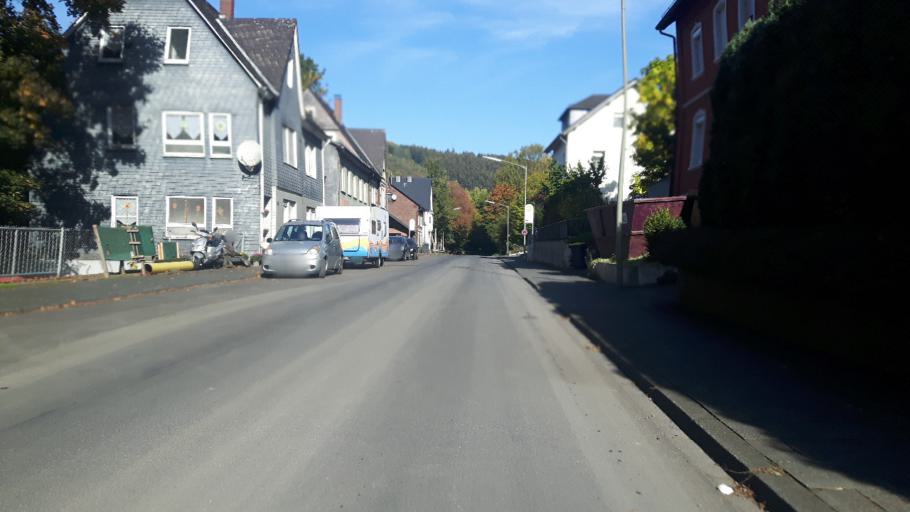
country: DE
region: North Rhine-Westphalia
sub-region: Regierungsbezirk Arnsberg
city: Siegen
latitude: 50.9090
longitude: 8.0377
